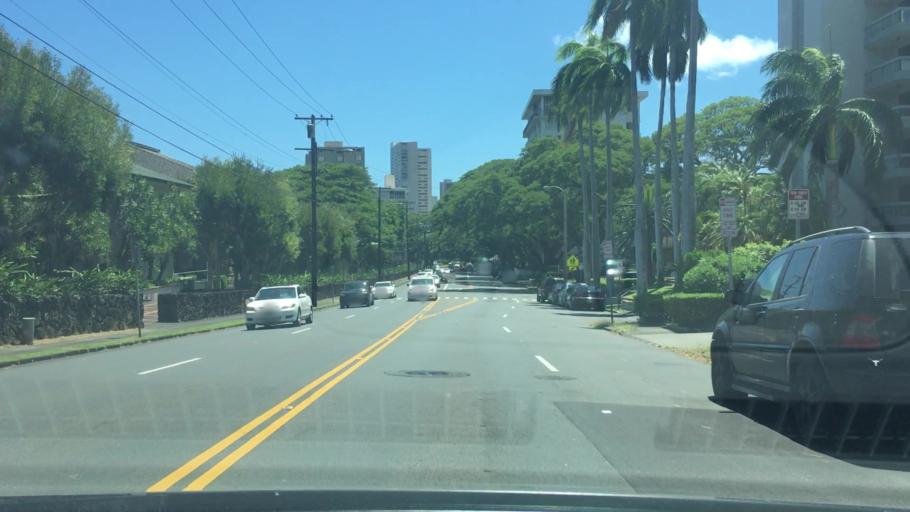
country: US
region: Hawaii
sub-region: Honolulu County
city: Honolulu
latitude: 21.3046
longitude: -157.8308
